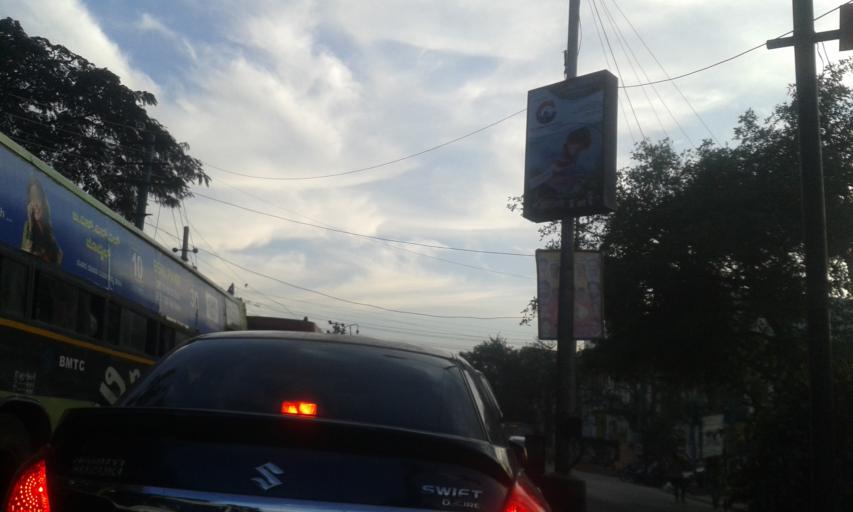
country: IN
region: Karnataka
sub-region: Bangalore Rural
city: Hoskote
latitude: 12.9842
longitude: 77.7527
